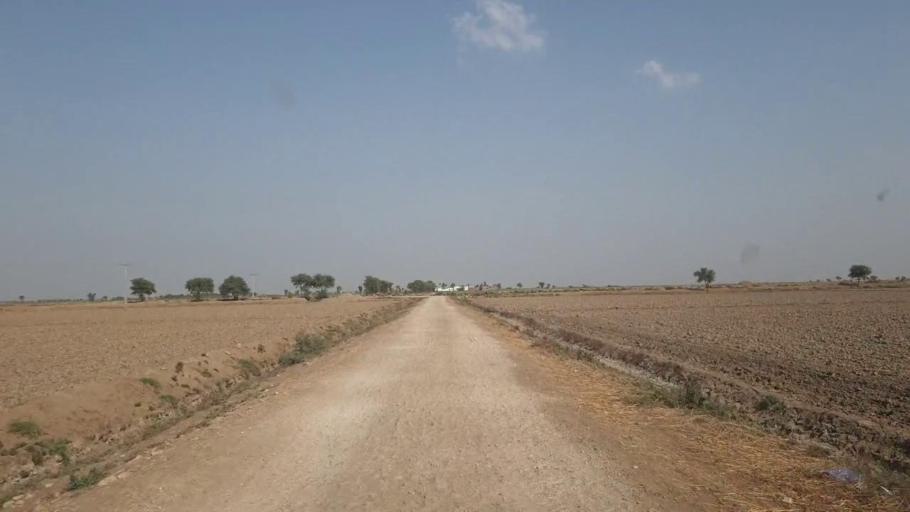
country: PK
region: Sindh
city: Kario
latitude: 24.5530
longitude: 68.5345
